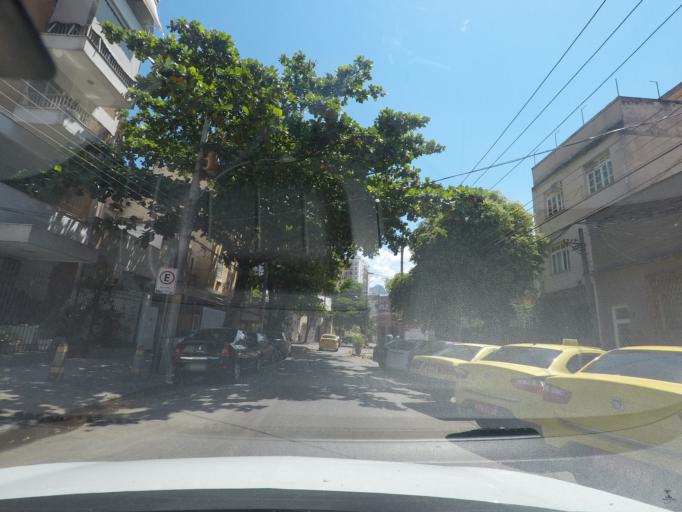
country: BR
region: Rio de Janeiro
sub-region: Rio De Janeiro
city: Rio de Janeiro
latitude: -22.9179
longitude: -43.2357
